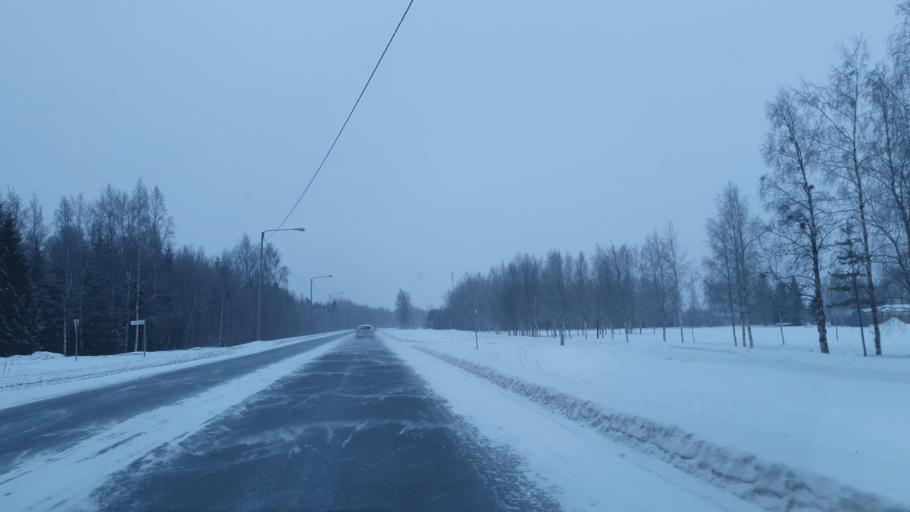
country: FI
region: Lapland
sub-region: Kemi-Tornio
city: Tornio
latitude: 65.8759
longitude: 24.1599
